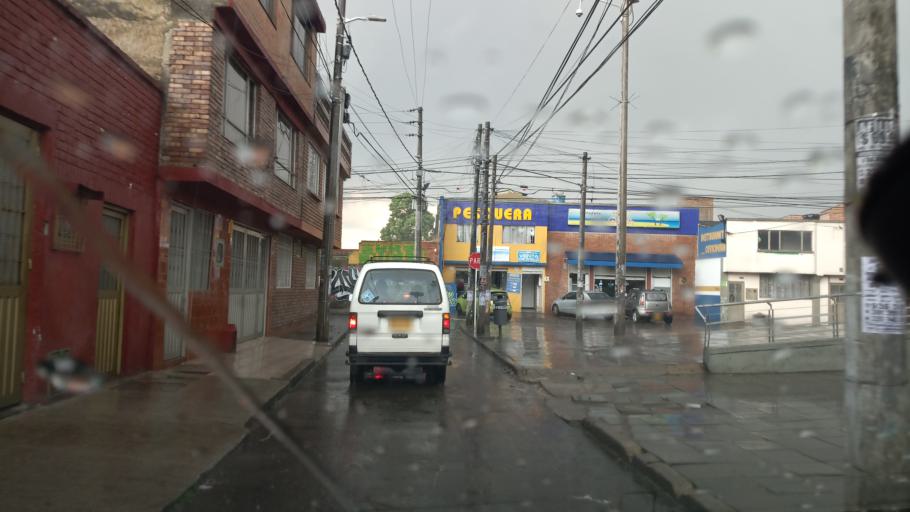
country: CO
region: Cundinamarca
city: Funza
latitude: 4.6730
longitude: -74.1397
